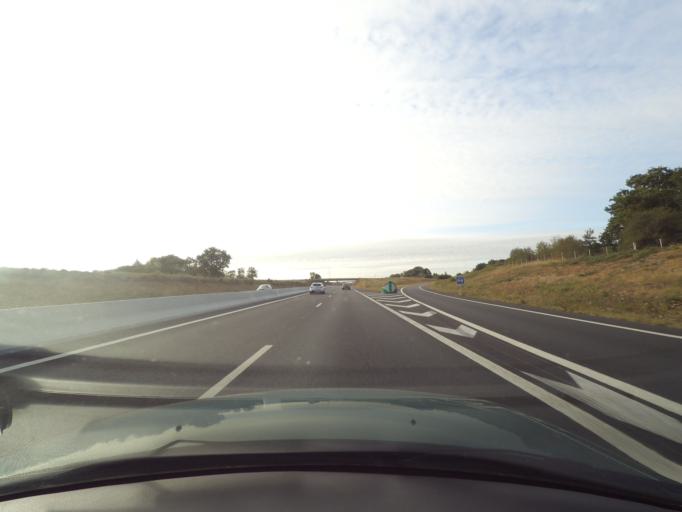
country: FR
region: Pays de la Loire
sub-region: Departement de Maine-et-Loire
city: Cholet
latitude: 47.0258
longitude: -0.8870
